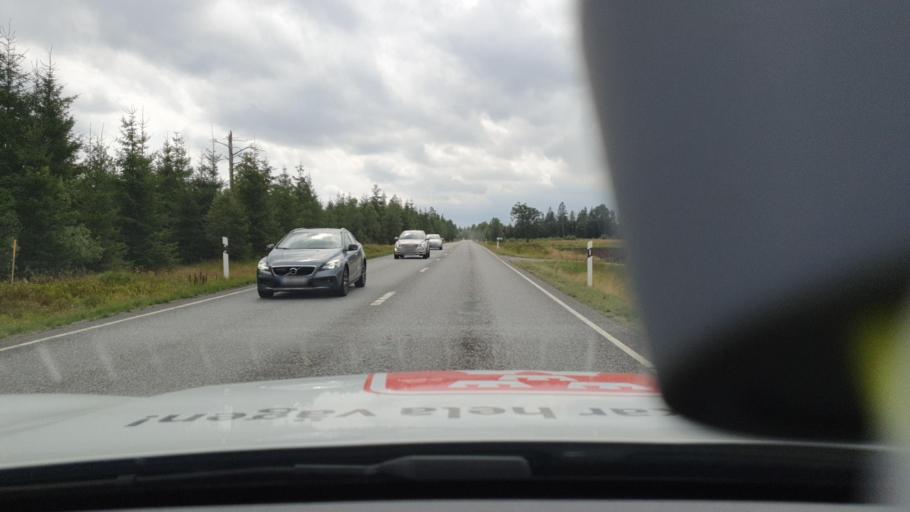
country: SE
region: Joenkoeping
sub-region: Gislaveds Kommun
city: Smalandsstenar
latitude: 57.2279
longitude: 13.4394
